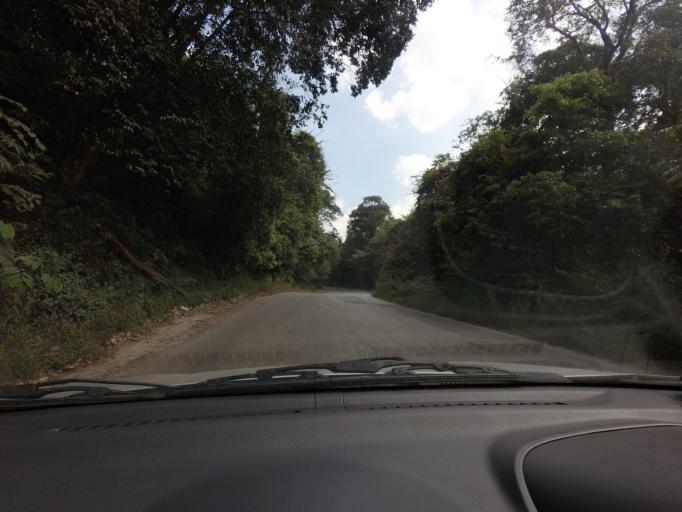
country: IN
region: Karnataka
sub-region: Hassan
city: Sakleshpur
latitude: 12.8293
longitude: 75.6233
